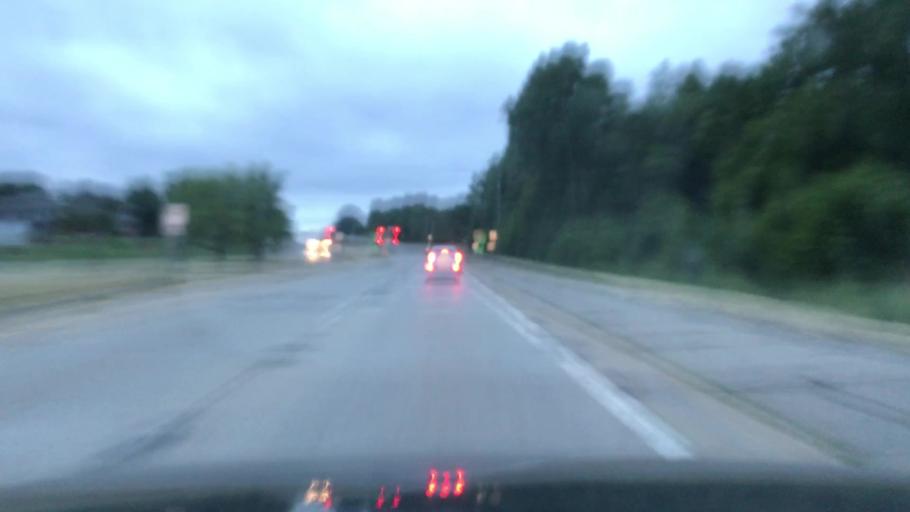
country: US
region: Michigan
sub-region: Kent County
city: East Grand Rapids
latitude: 42.9408
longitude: -85.5852
